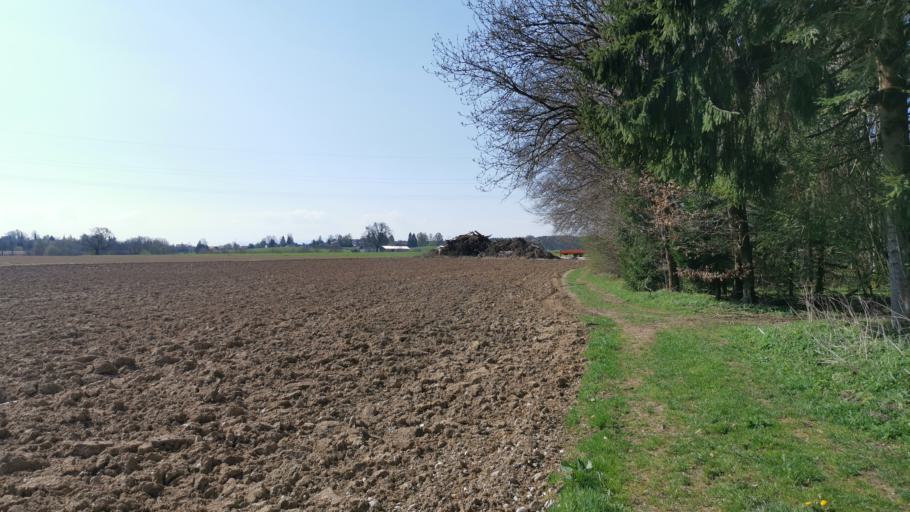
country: DE
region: Bavaria
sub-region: Upper Bavaria
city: Schaftlarn
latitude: 47.9979
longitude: 11.4411
